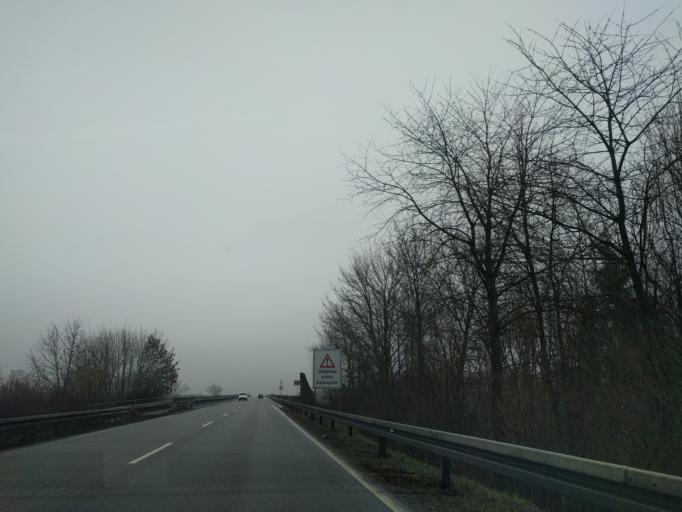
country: DE
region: Bavaria
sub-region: Lower Bavaria
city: Winzer
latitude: 48.7207
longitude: 13.0540
